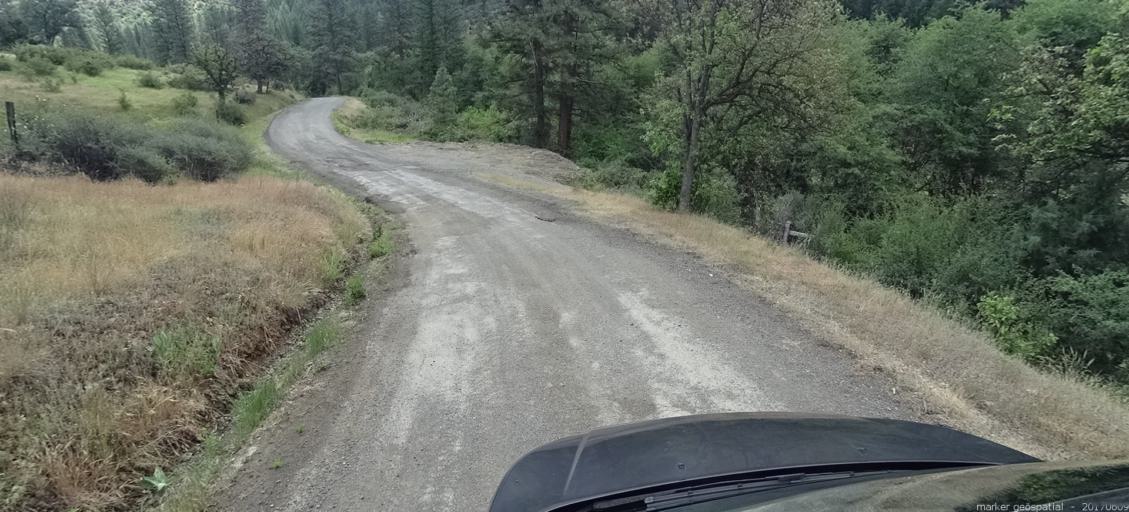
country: US
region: California
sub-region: Siskiyou County
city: Weed
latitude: 41.3099
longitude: -122.8277
